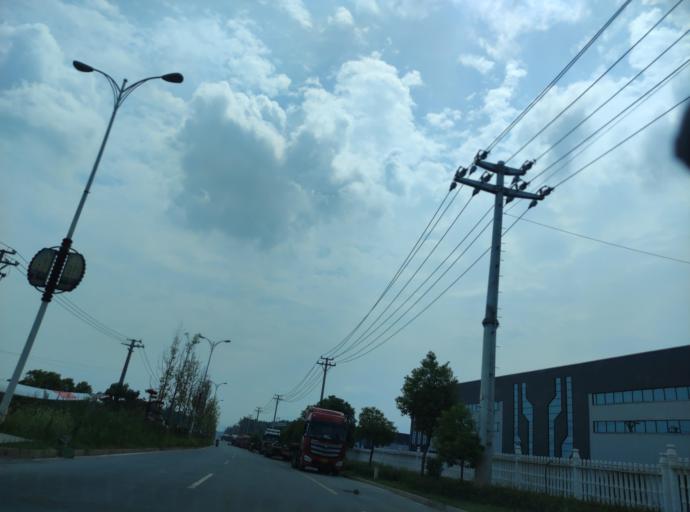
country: CN
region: Jiangxi Sheng
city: Yuannan
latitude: 27.6640
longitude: 114.0213
